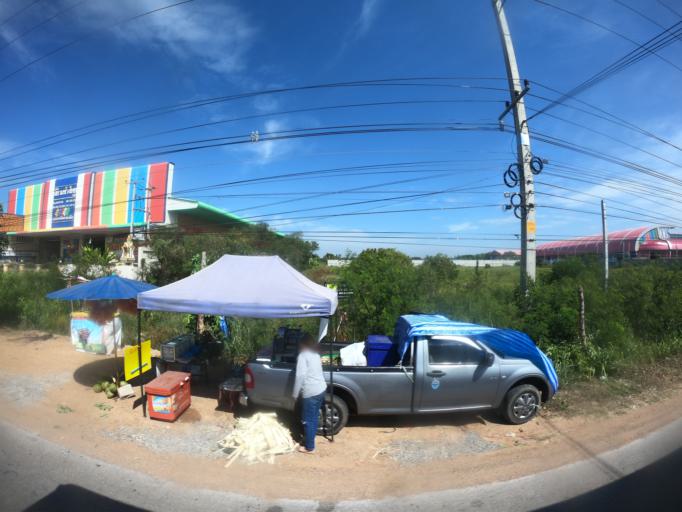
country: TH
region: Khon Kaen
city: Khon Kaen
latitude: 16.4377
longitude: 102.9220
